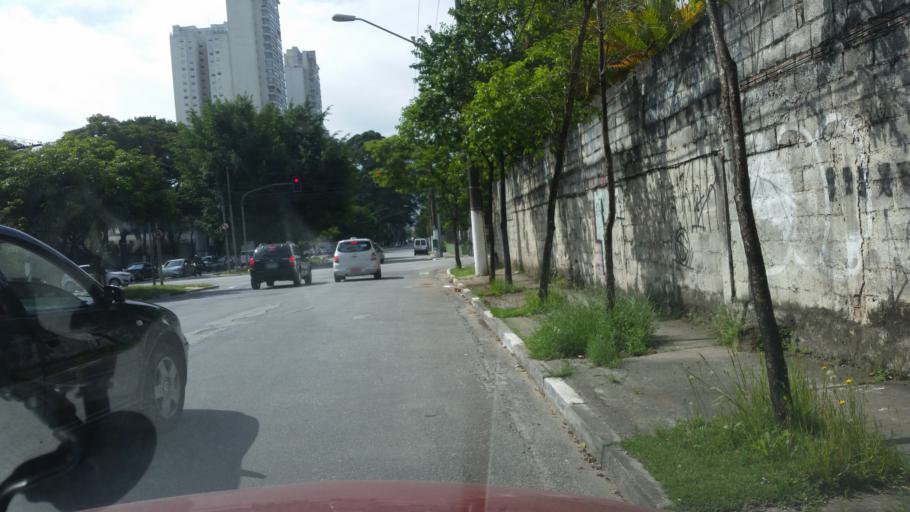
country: BR
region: Sao Paulo
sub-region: Diadema
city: Diadema
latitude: -23.6717
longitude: -46.6999
